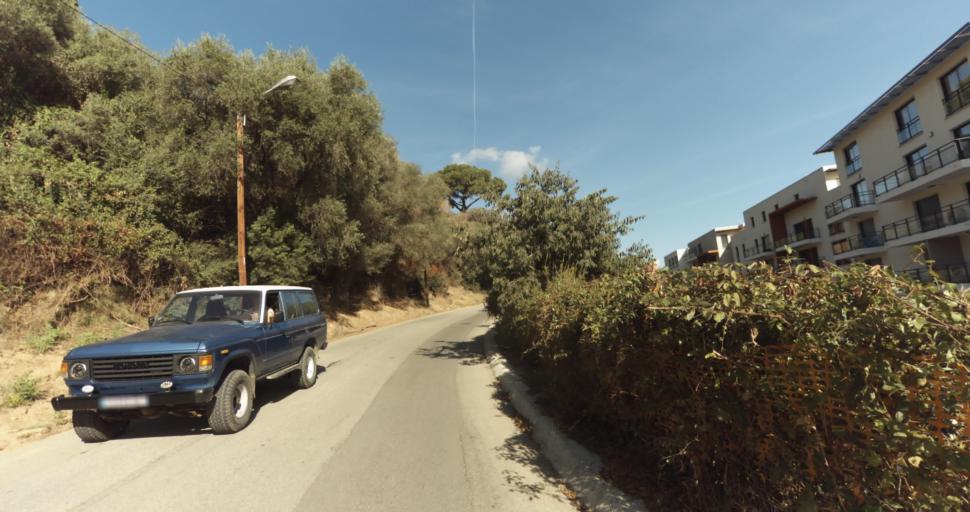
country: FR
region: Corsica
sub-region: Departement de la Corse-du-Sud
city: Ajaccio
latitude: 41.9237
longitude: 8.7294
